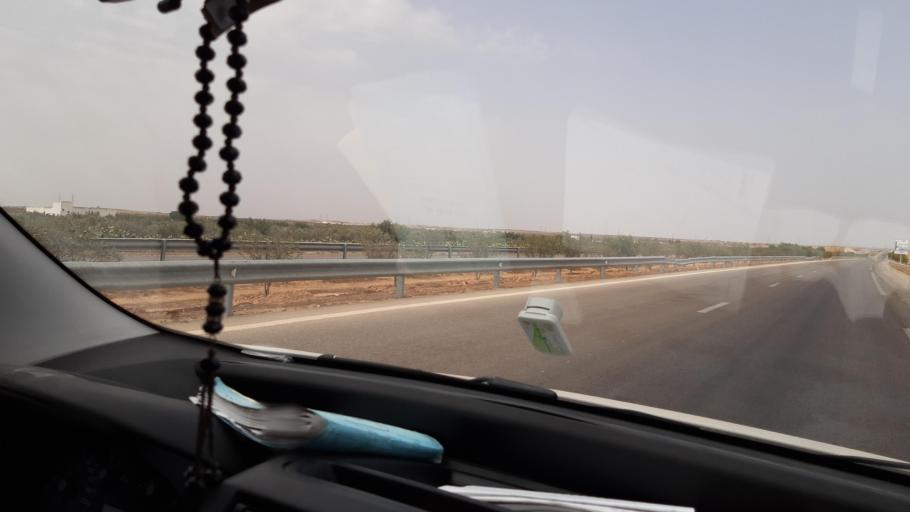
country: TN
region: Safaqis
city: Sfax
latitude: 34.8770
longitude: 10.6995
